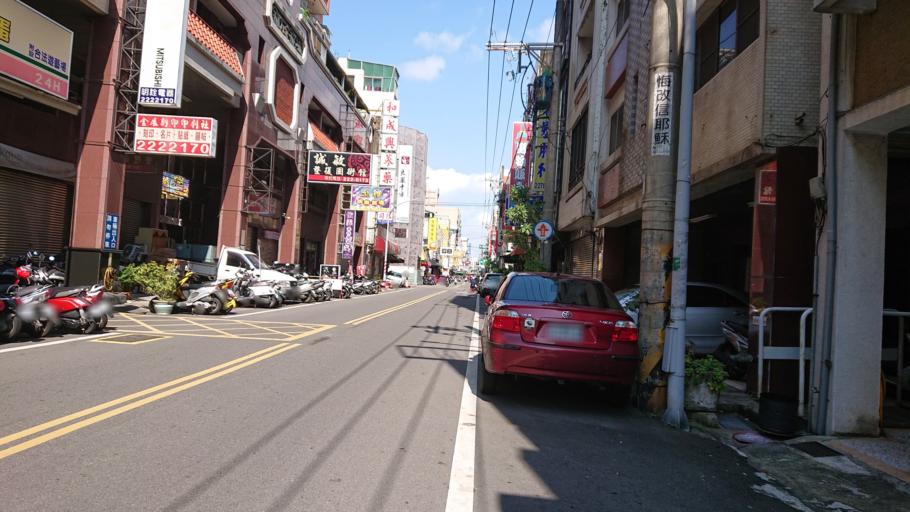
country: TW
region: Taiwan
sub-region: Chiayi
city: Jiayi Shi
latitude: 23.4764
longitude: 120.4445
